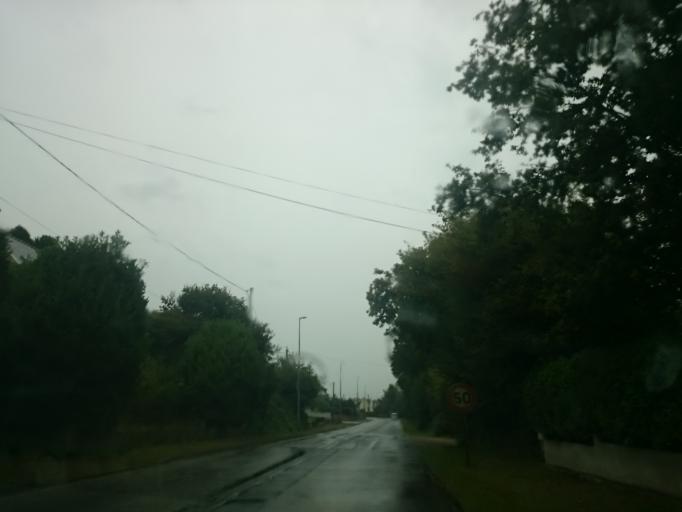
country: FR
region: Brittany
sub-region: Departement du Finistere
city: Le Drennec
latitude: 48.5307
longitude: -4.3763
